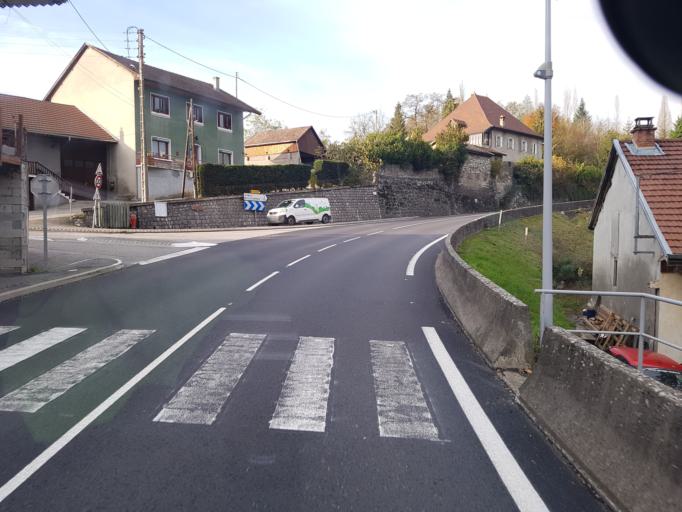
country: FR
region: Rhone-Alpes
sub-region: Departement de la Haute-Savoie
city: Frangy
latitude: 46.0290
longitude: 5.8884
